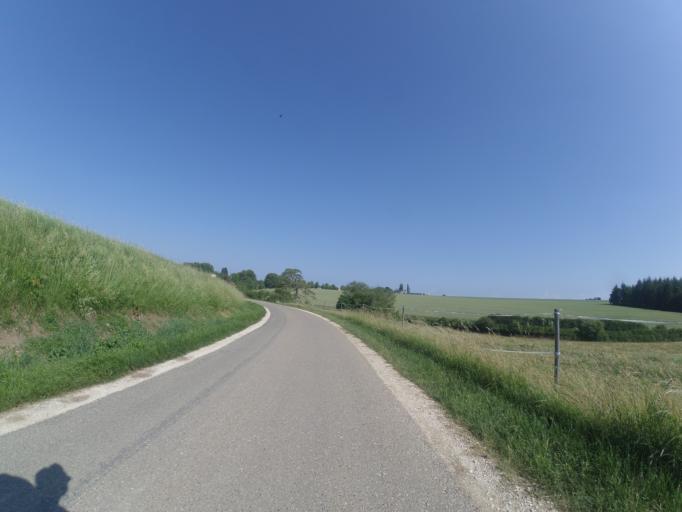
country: DE
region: Baden-Wuerttemberg
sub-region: Tuebingen Region
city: Beimerstetten
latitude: 48.4727
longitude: 9.9927
